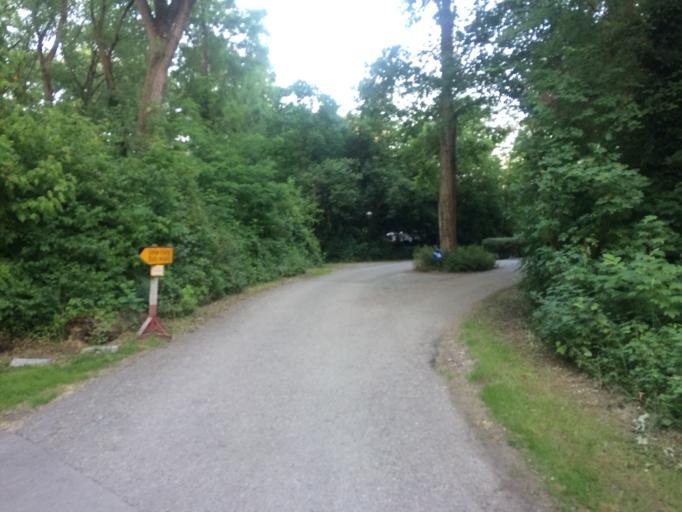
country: AT
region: Lower Austria
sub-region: Politischer Bezirk Tulln
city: Tulln
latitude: 48.3312
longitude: 16.0402
